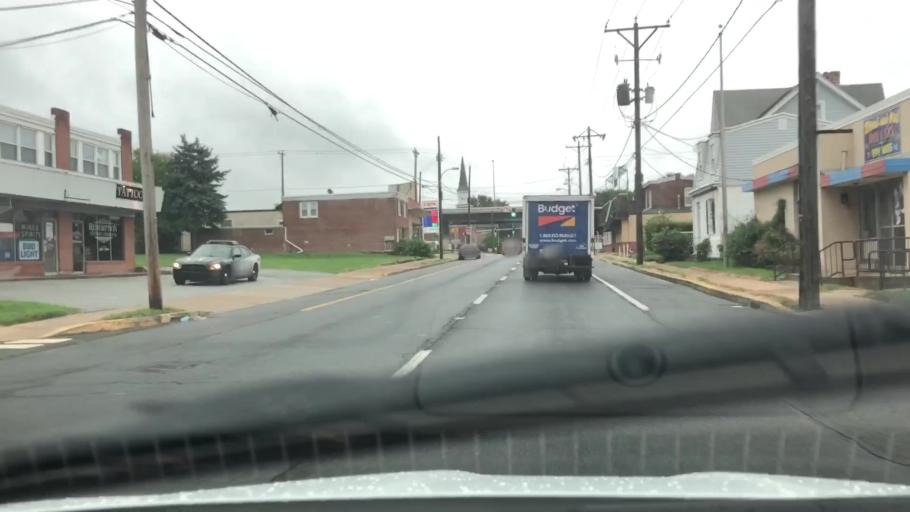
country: US
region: Delaware
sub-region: New Castle County
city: Newport
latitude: 39.7136
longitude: -75.6107
